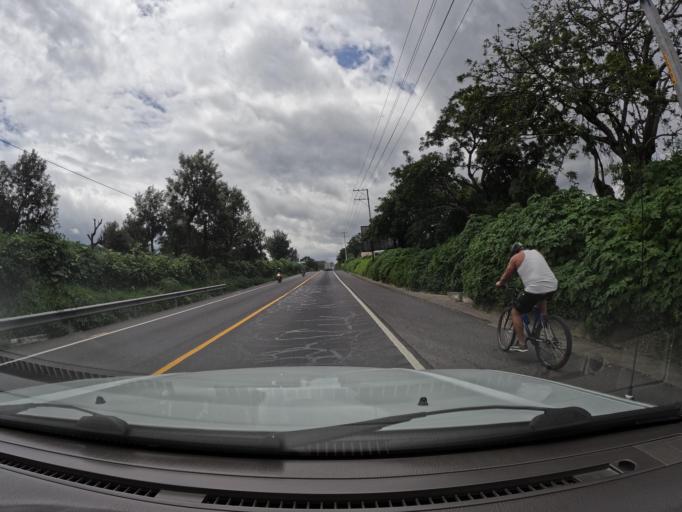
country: GT
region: Sacatepequez
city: San Miguel Duenas
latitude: 14.5041
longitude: -90.7919
